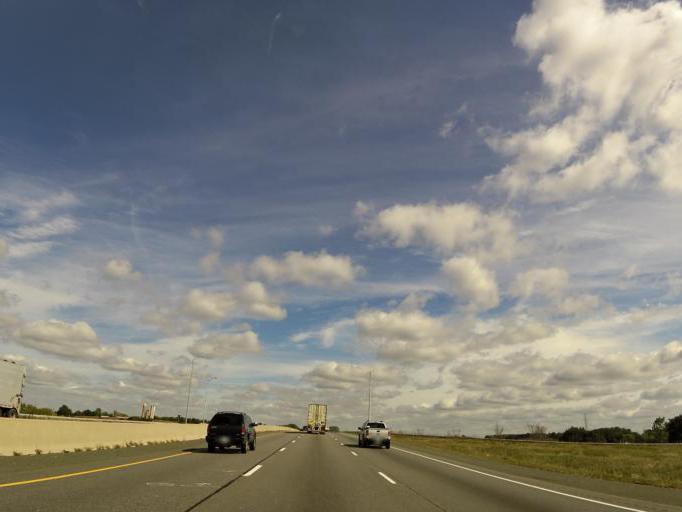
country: CA
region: Ontario
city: Ingersoll
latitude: 42.9754
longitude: -80.9528
